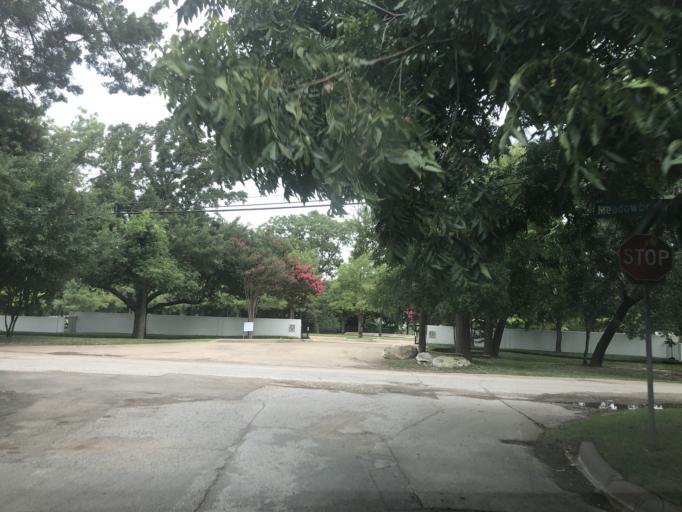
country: US
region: Texas
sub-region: Dallas County
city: University Park
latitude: 32.8664
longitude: -96.8183
